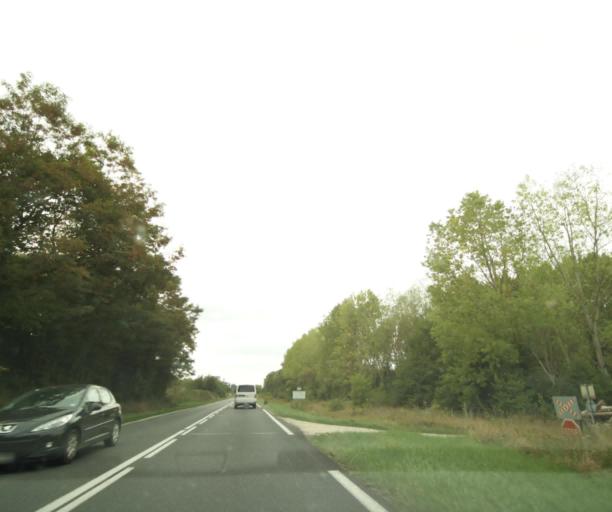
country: FR
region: Centre
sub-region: Departement d'Indre-et-Loire
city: Perrusson
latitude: 47.0737
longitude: 1.0685
